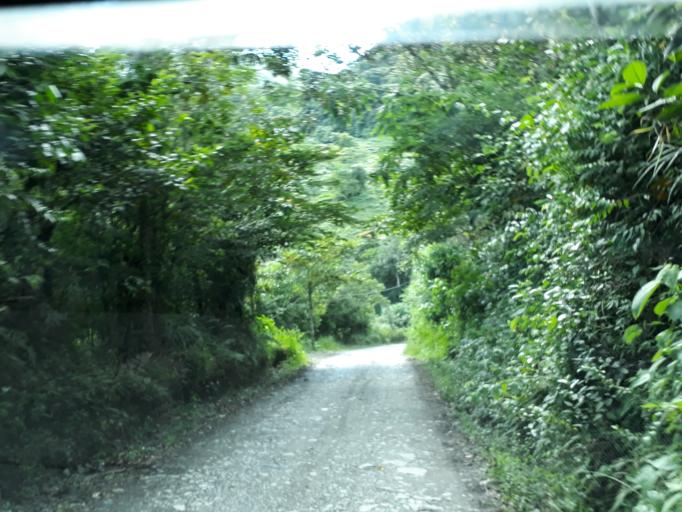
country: CO
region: Cundinamarca
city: Topaipi
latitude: 5.3828
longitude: -74.1952
